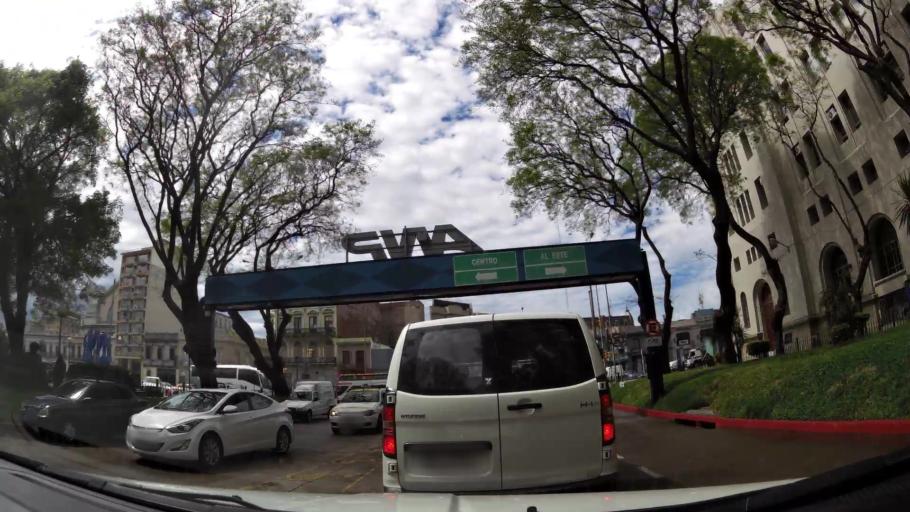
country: UY
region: Montevideo
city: Montevideo
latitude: -34.9044
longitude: -56.2114
